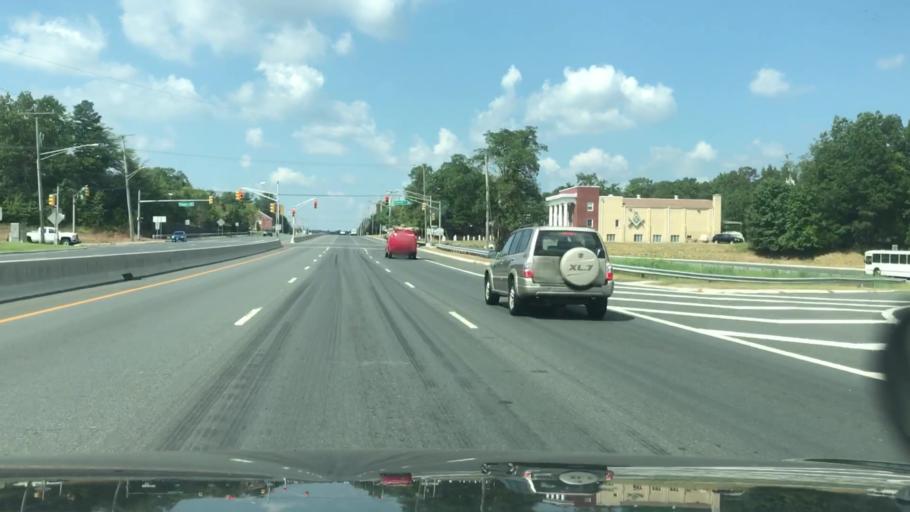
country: US
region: New Jersey
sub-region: Ocean County
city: Silver Ridge
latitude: 39.9654
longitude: -74.2160
